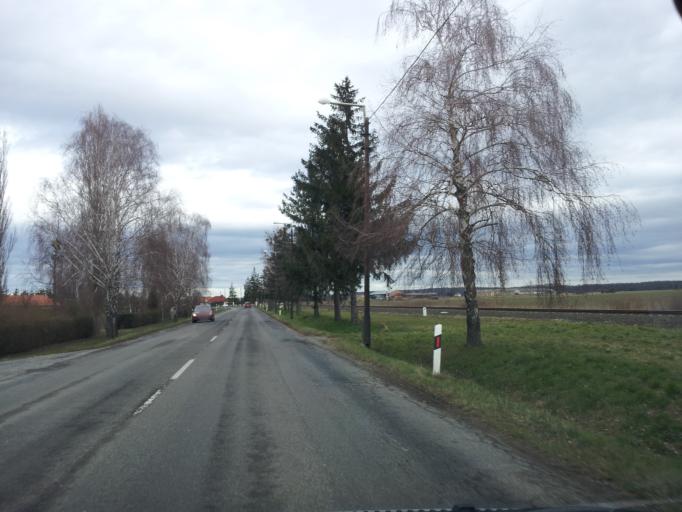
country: HU
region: Vas
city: Gencsapati
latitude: 47.3336
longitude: 16.5829
